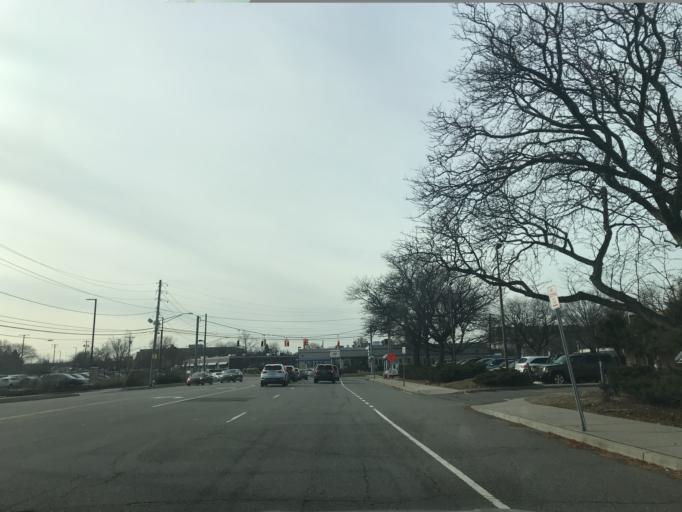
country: US
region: New York
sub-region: Nassau County
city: East Garden City
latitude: 40.7399
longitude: -73.6045
